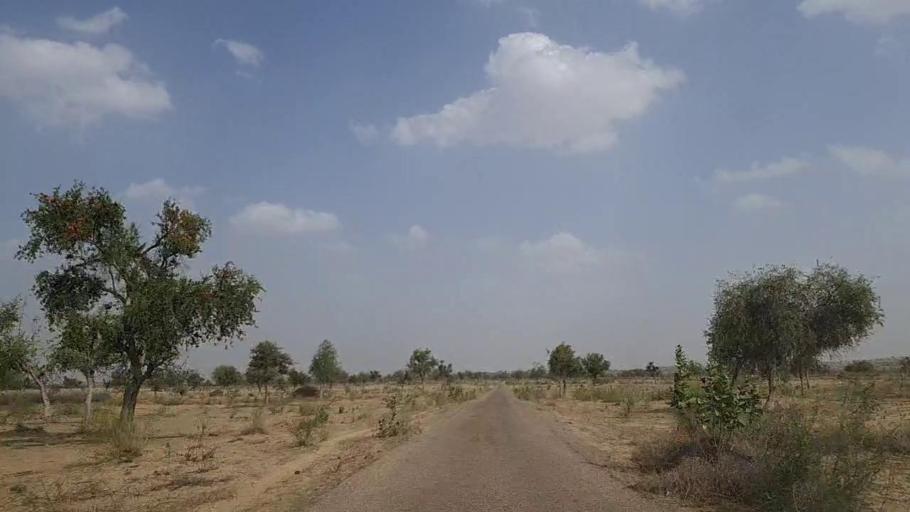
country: PK
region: Sindh
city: Islamkot
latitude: 24.8298
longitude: 70.1622
